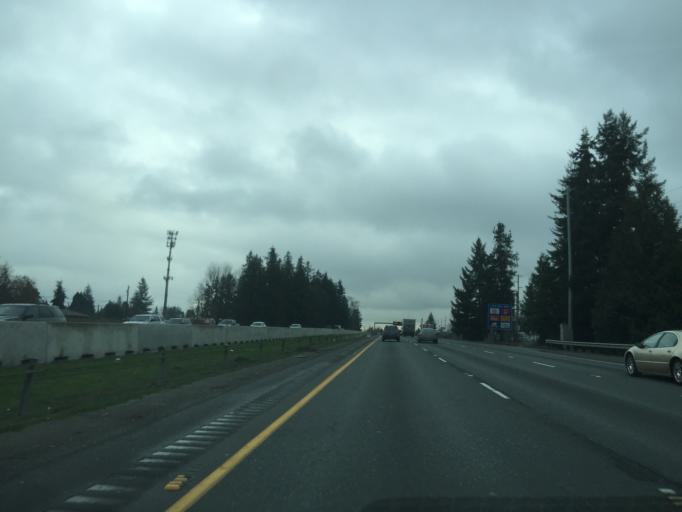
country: US
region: Washington
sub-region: Snohomish County
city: Marysville
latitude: 48.0633
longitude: -122.1850
